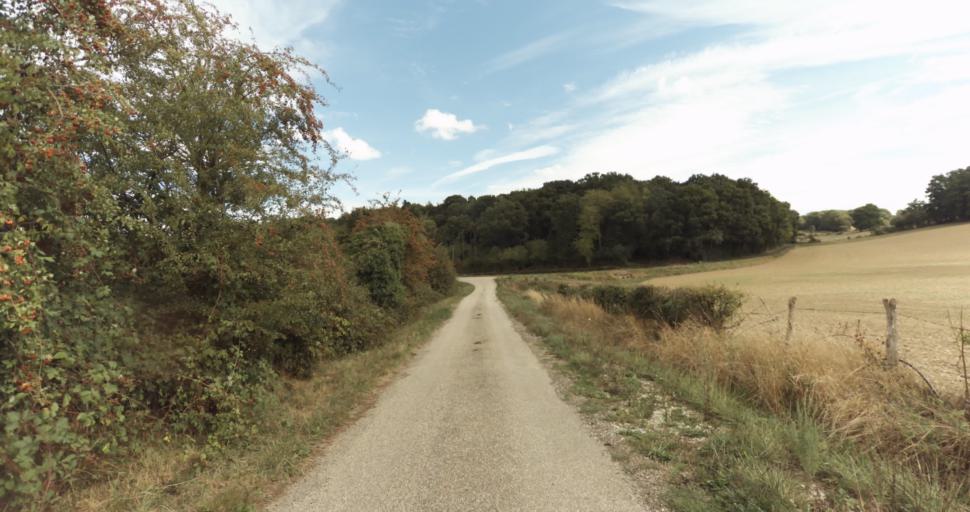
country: FR
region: Lower Normandy
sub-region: Departement du Calvados
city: Orbec
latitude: 48.9123
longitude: 0.3822
